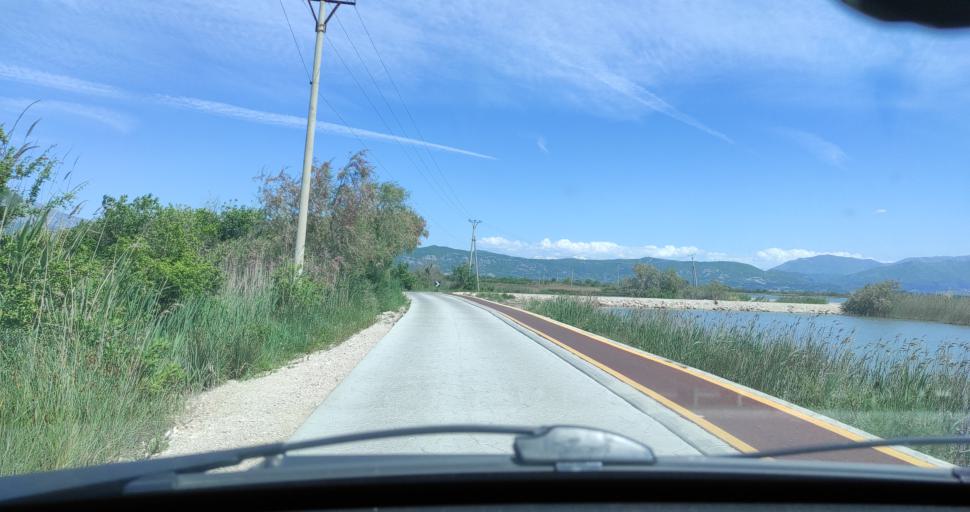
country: AL
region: Lezhe
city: Shengjin
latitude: 41.7465
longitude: 19.5860
